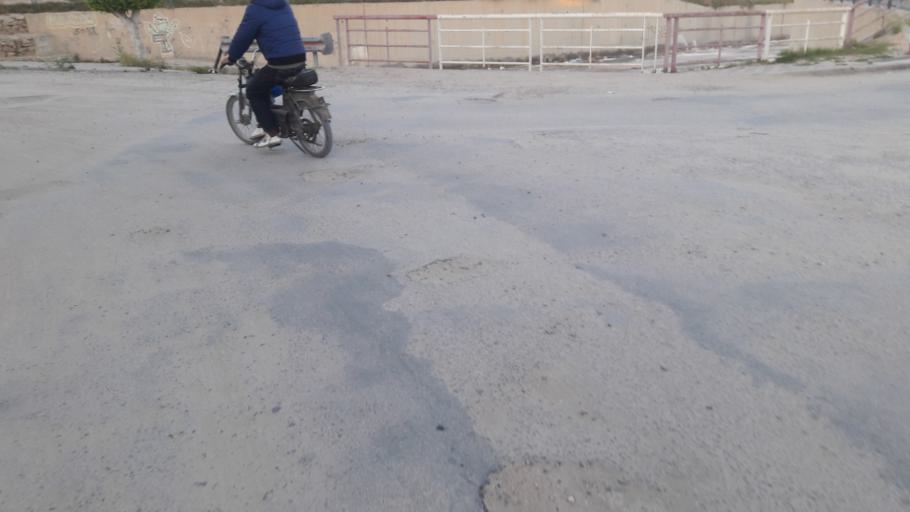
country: TN
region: Safaqis
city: Al Qarmadah
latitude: 34.8084
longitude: 10.7502
